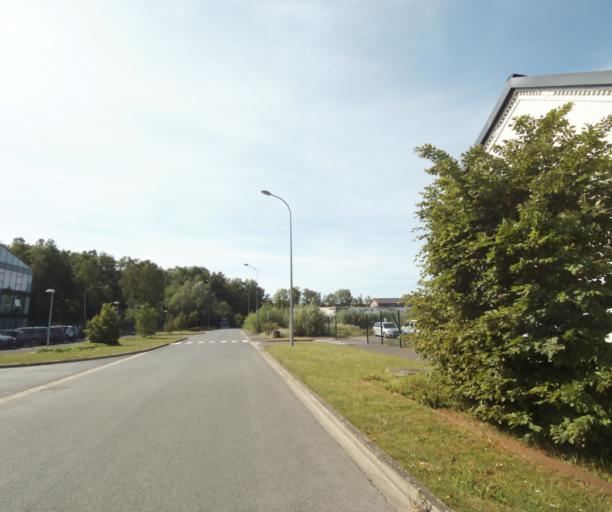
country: FR
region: Champagne-Ardenne
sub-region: Departement des Ardennes
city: Villers-Semeuse
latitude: 49.7430
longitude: 4.7306
